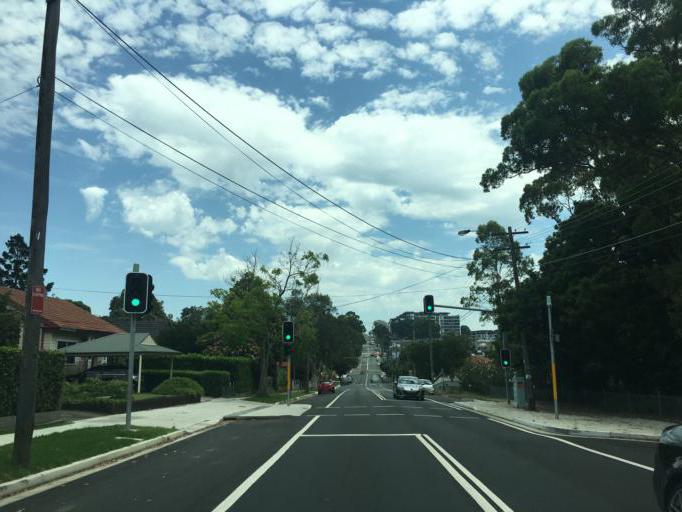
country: AU
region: New South Wales
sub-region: Canada Bay
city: Rhodes
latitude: -33.8250
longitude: 151.1103
